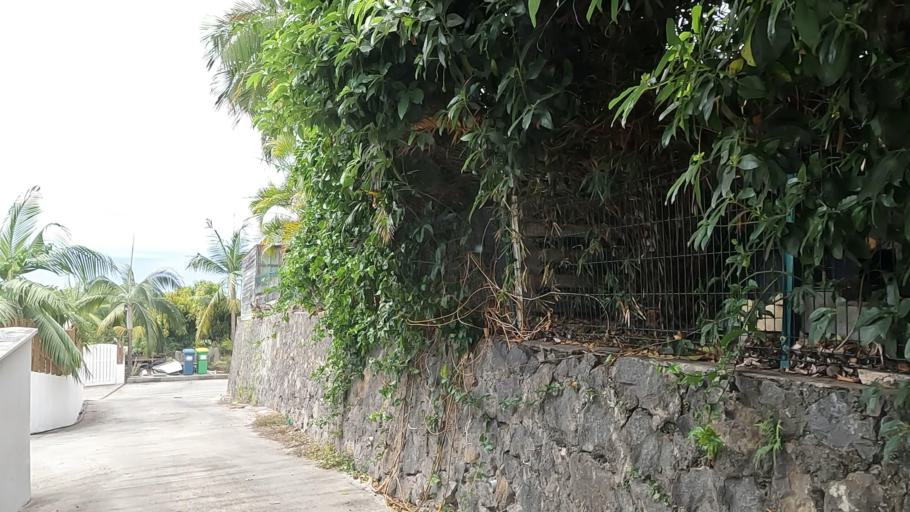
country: RE
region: Reunion
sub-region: Reunion
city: Saint-Paul
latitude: -21.0204
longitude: 55.2873
